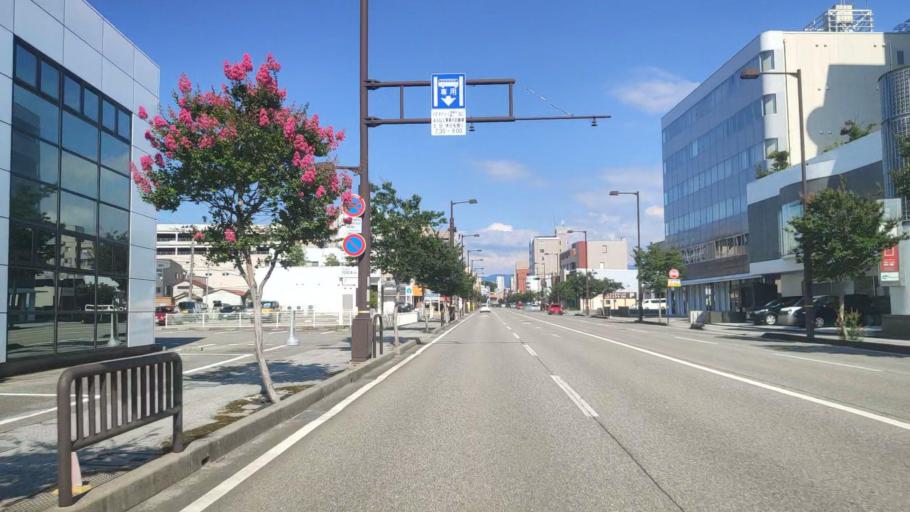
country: JP
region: Ishikawa
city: Nonoichi
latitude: 36.5589
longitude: 136.6402
